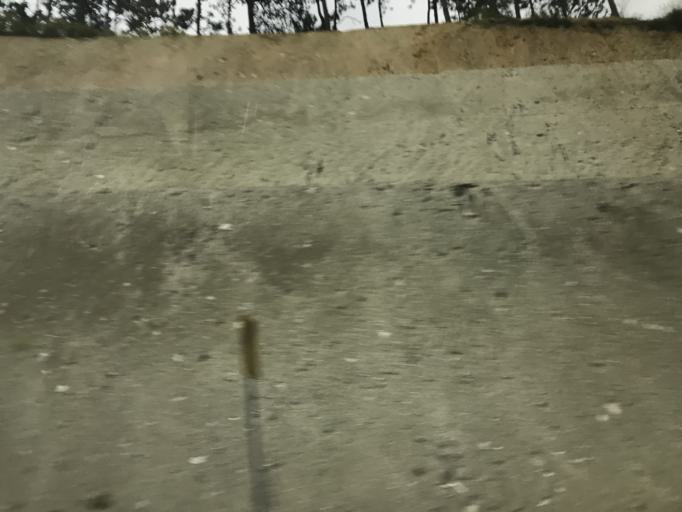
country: GT
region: Chimaltenango
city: El Tejar
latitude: 14.6379
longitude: -90.7933
